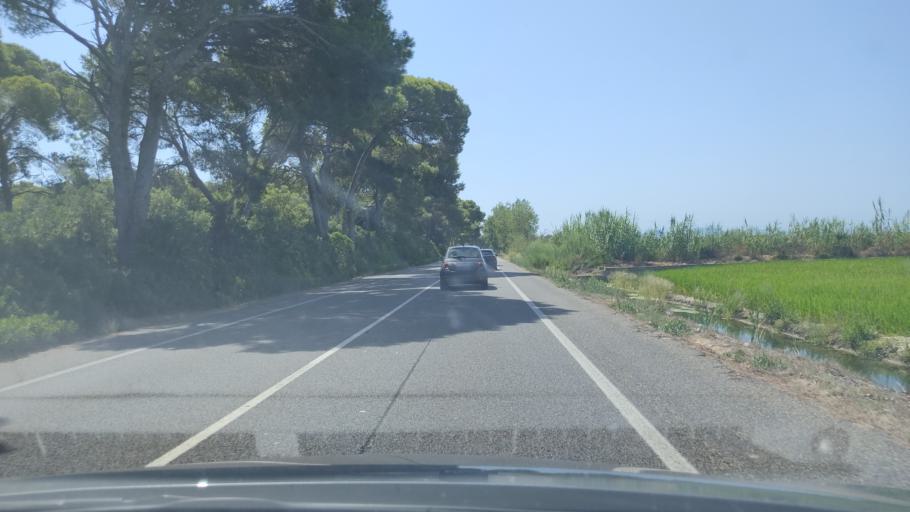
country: ES
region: Valencia
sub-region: Provincia de Valencia
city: Alfafar
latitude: 39.3694
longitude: -0.3295
